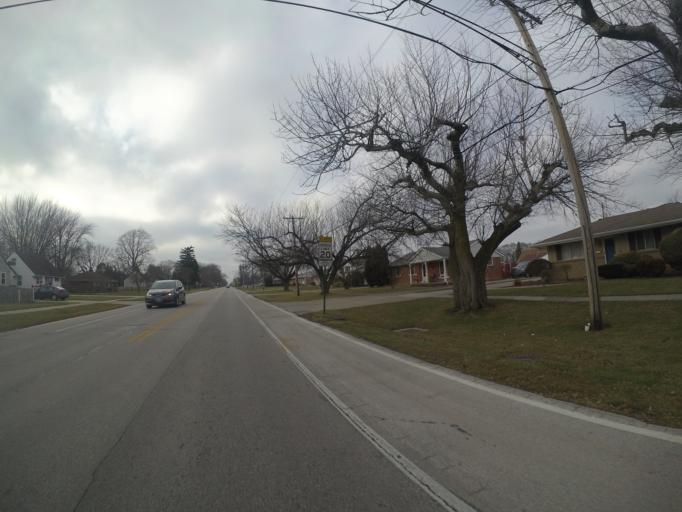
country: US
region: Ohio
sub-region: Lucas County
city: Oregon
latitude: 41.6443
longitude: -83.4721
